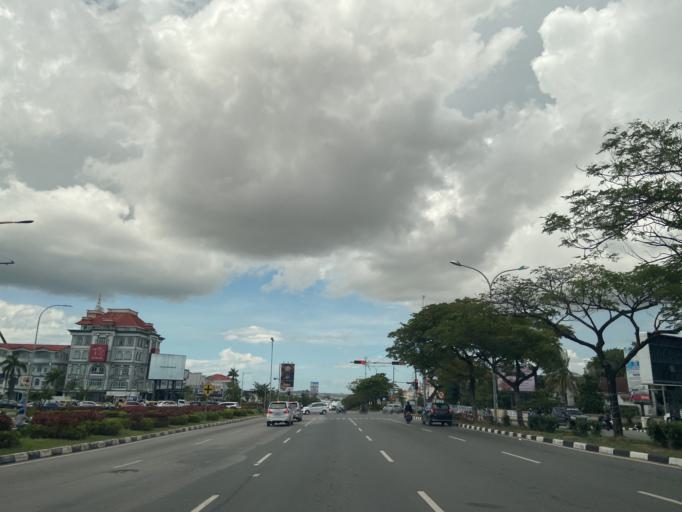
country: SG
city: Singapore
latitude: 1.1261
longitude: 104.0307
